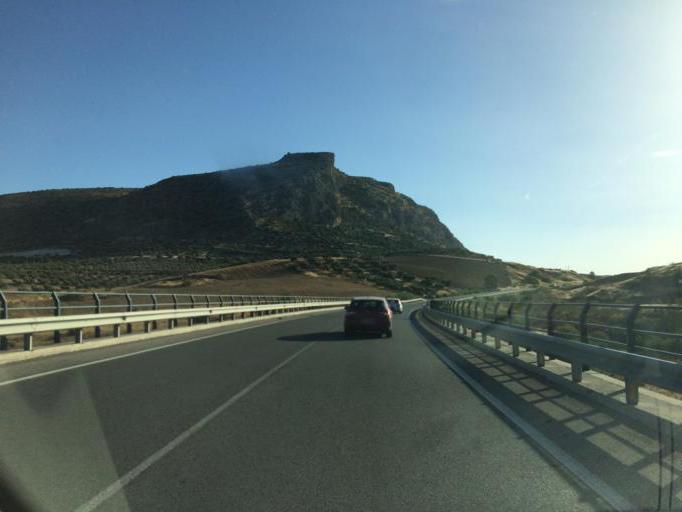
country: ES
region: Andalusia
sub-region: Provincia de Malaga
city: Teba
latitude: 36.9611
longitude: -4.8572
